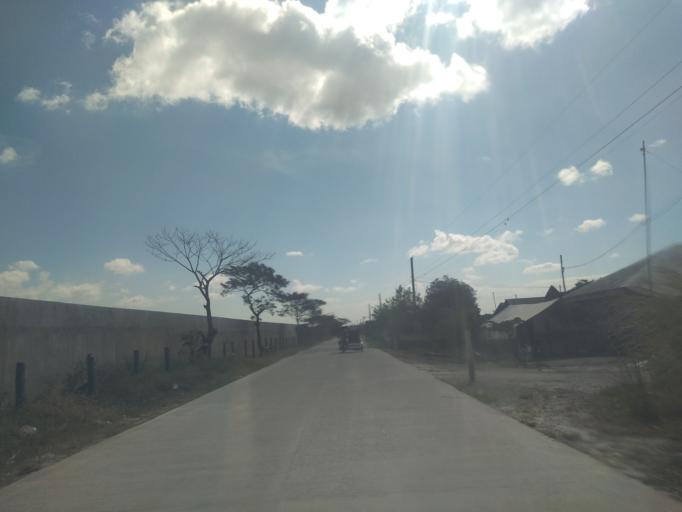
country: PH
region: Central Luzon
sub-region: Province of Pampanga
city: Balas
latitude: 15.0564
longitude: 120.6010
